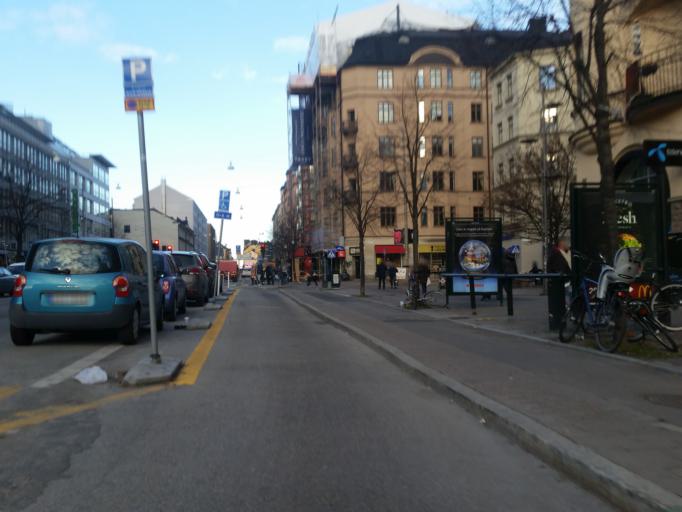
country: SE
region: Stockholm
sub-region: Stockholms Kommun
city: Stockholm
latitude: 59.3117
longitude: 18.0745
